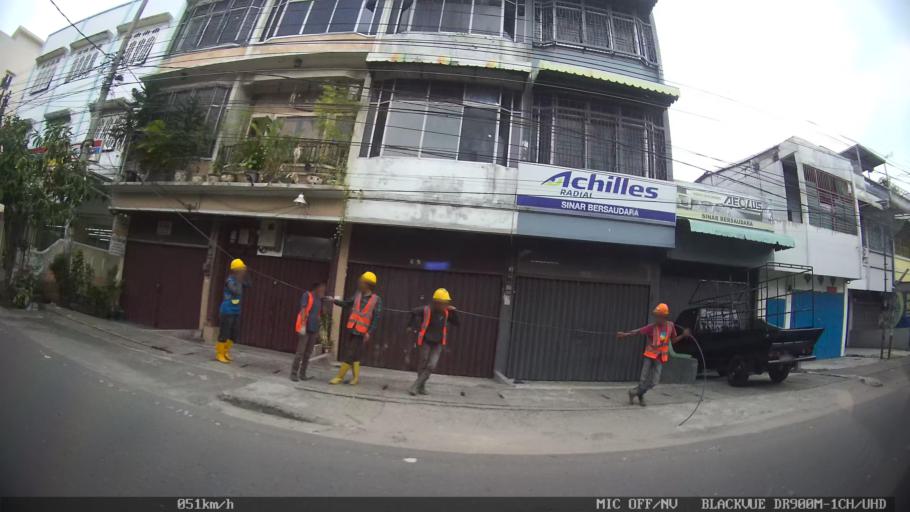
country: ID
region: North Sumatra
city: Medan
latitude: 3.5666
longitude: 98.6883
